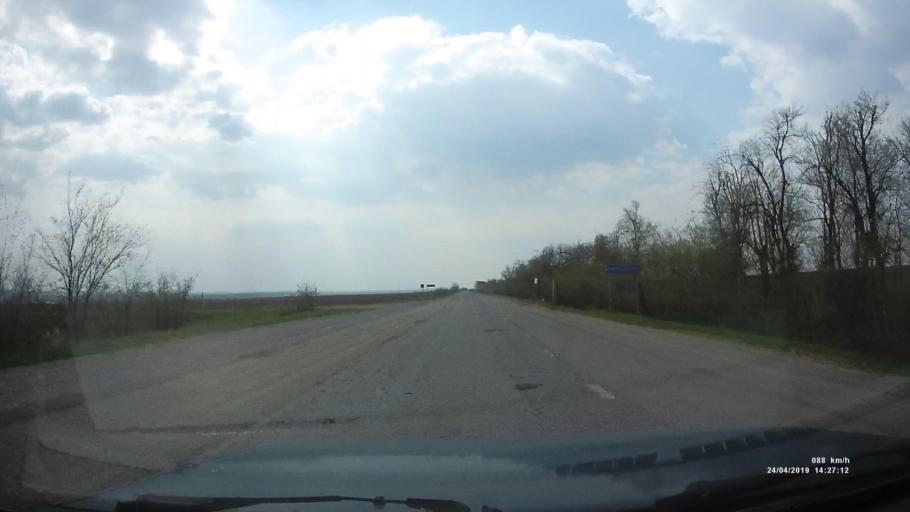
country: RU
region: Kalmykiya
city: Arshan'
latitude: 46.3341
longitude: 44.0475
